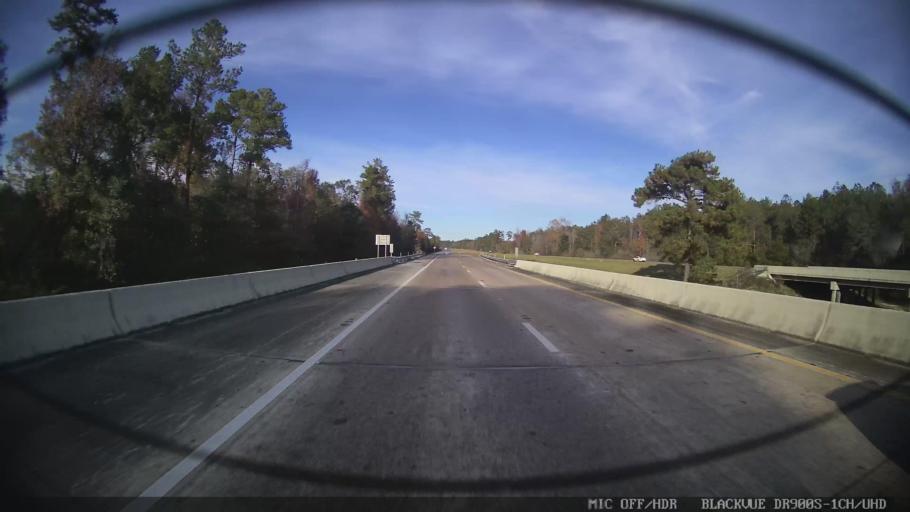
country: US
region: Mississippi
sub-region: Lamar County
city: Purvis
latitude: 31.1696
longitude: -89.3521
